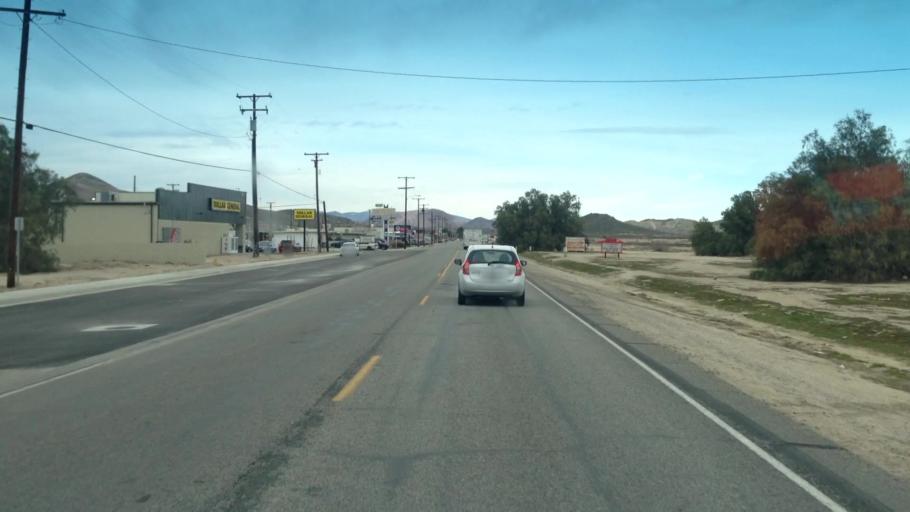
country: US
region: California
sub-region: Kern County
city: Rosamond
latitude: 34.8560
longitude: -118.1621
